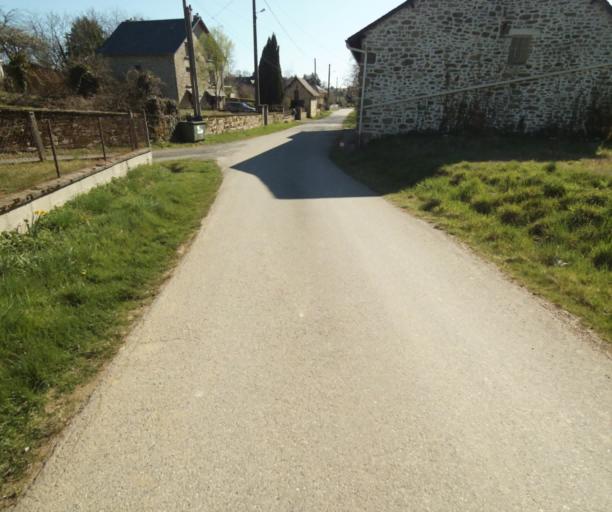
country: FR
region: Limousin
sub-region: Departement de la Correze
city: Chamboulive
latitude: 45.4706
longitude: 1.7349
